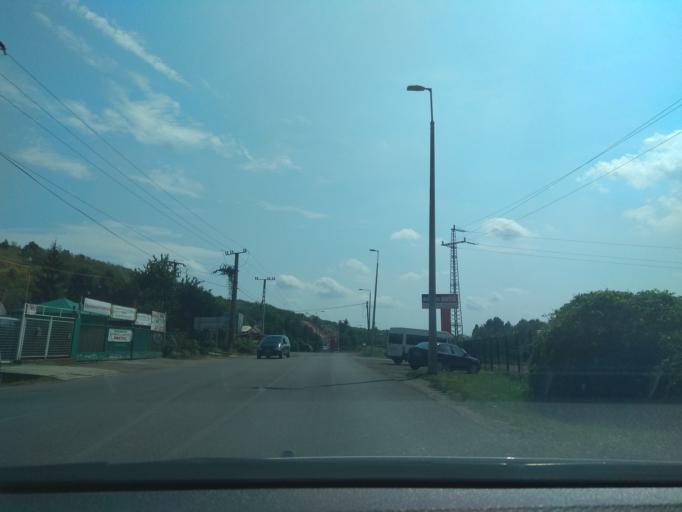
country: HU
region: Heves
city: Andornaktalya
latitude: 47.8722
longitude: 20.4032
